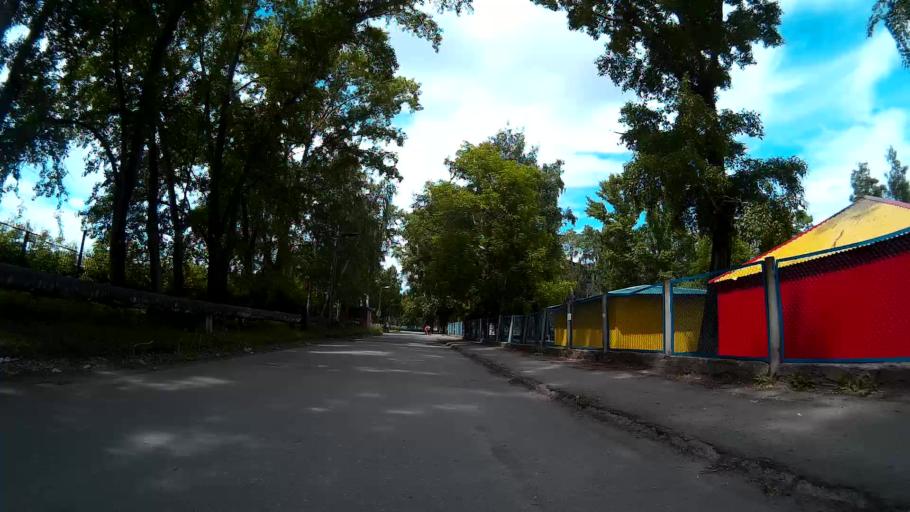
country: RU
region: Ulyanovsk
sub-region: Ulyanovskiy Rayon
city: Ulyanovsk
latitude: 54.2871
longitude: 48.3666
